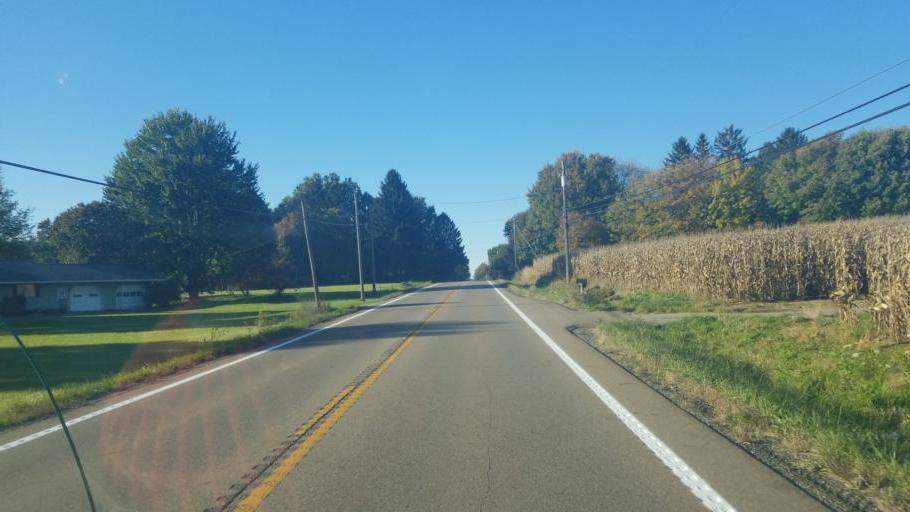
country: US
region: Ohio
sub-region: Columbiana County
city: New Waterford
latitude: 40.8288
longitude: -80.6388
